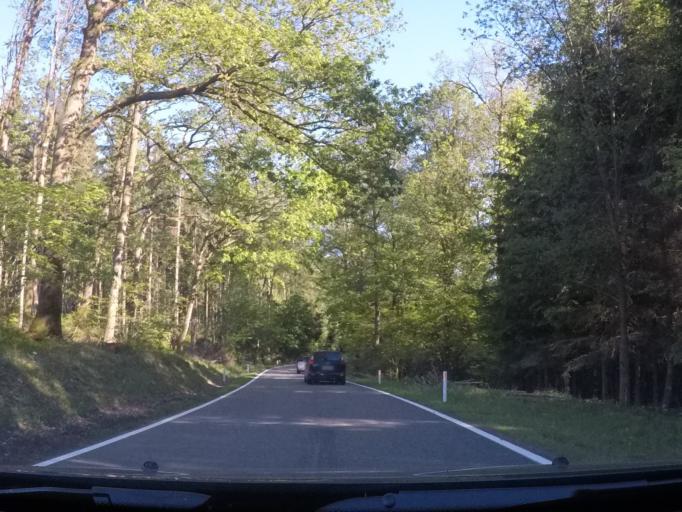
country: BE
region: Wallonia
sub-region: Province du Luxembourg
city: Saint-Hubert
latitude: 50.0396
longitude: 5.3567
